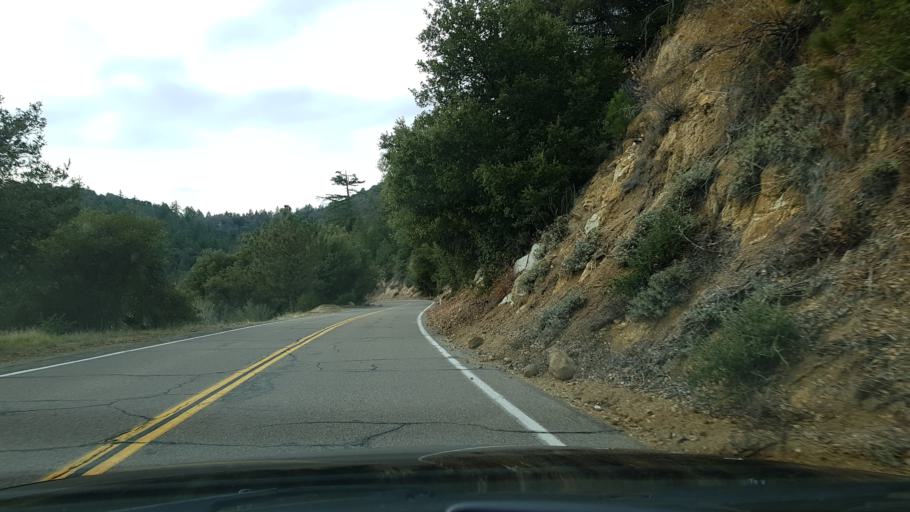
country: US
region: California
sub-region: Riverside County
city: Aguanga
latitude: 33.3444
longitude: -116.8746
